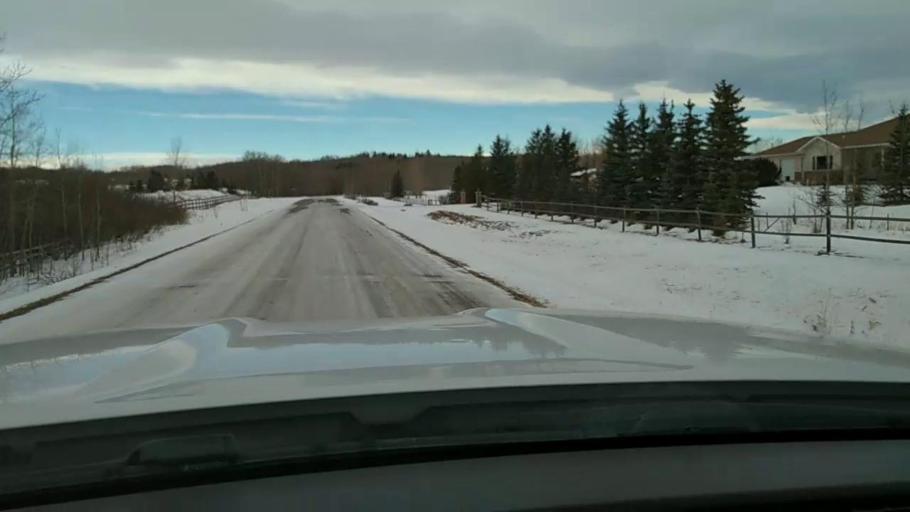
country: CA
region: Alberta
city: Cochrane
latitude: 51.1988
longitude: -114.2820
